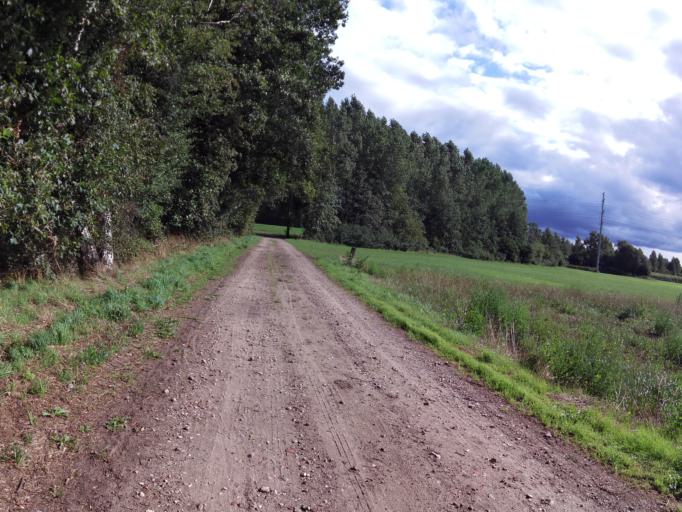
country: NL
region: Gelderland
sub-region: Gemeente Aalten
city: Bredevoort
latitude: 51.9547
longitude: 6.6307
